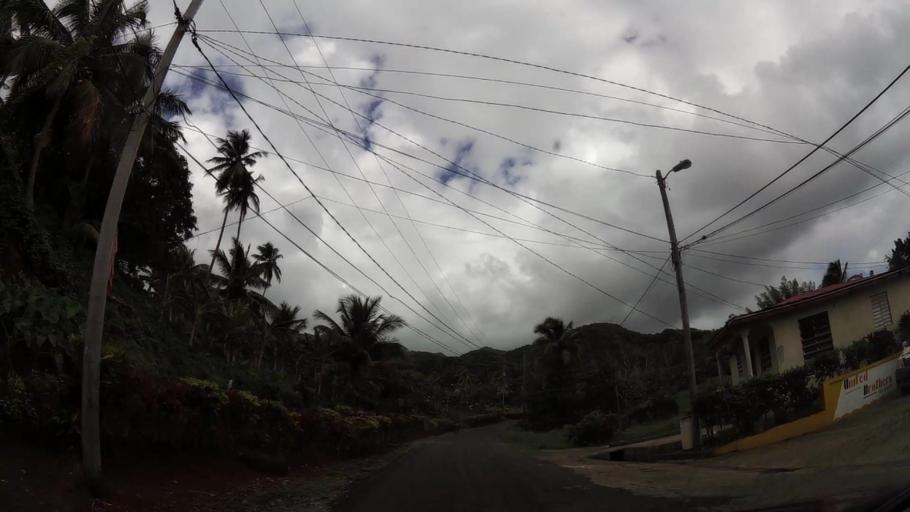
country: DM
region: Saint David
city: Castle Bruce
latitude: 15.4359
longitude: -61.2598
